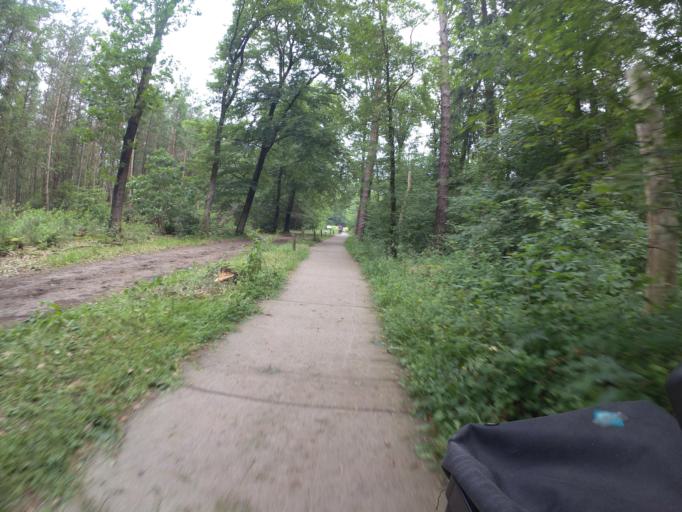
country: NL
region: Drenthe
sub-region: Gemeente Westerveld
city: Dwingeloo
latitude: 52.8111
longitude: 6.3551
